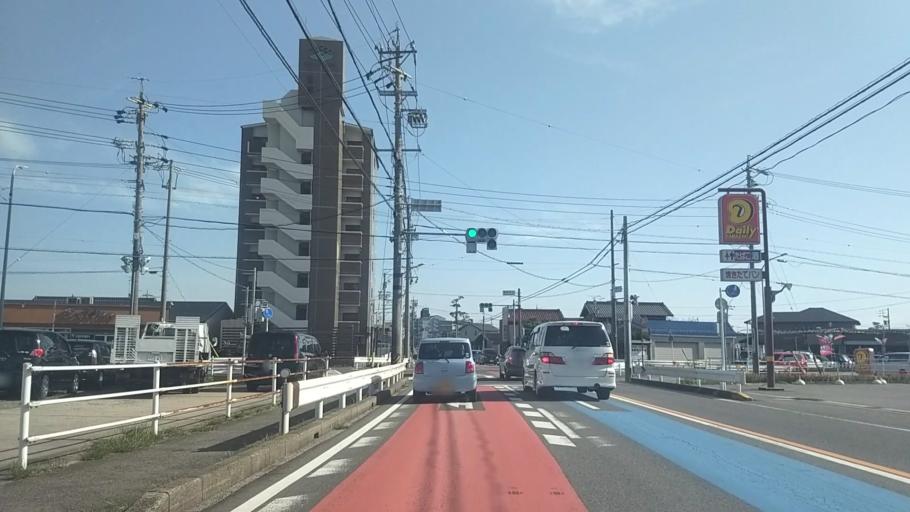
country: JP
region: Aichi
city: Anjo
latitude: 34.9591
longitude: 137.0577
